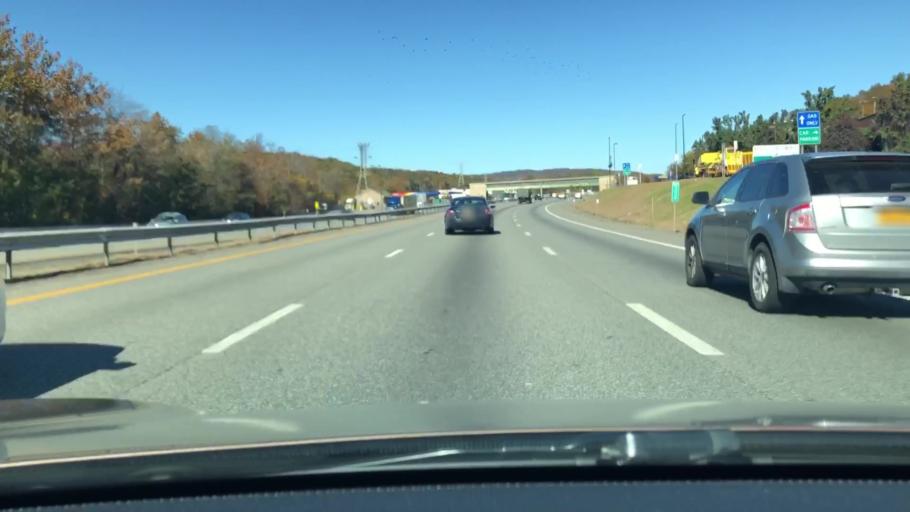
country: US
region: New York
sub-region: Rockland County
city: Sloatsburg
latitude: 41.1495
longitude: -74.1885
